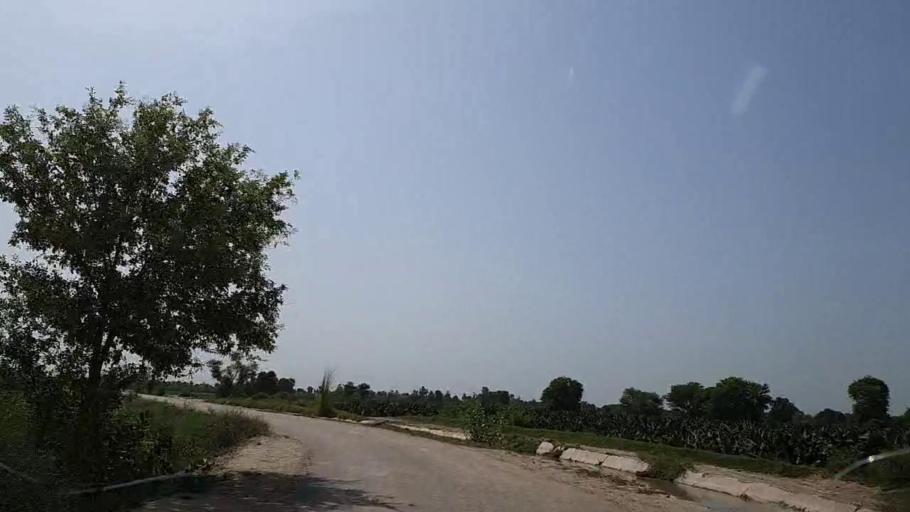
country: PK
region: Sindh
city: Kandiaro
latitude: 27.0503
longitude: 68.1624
